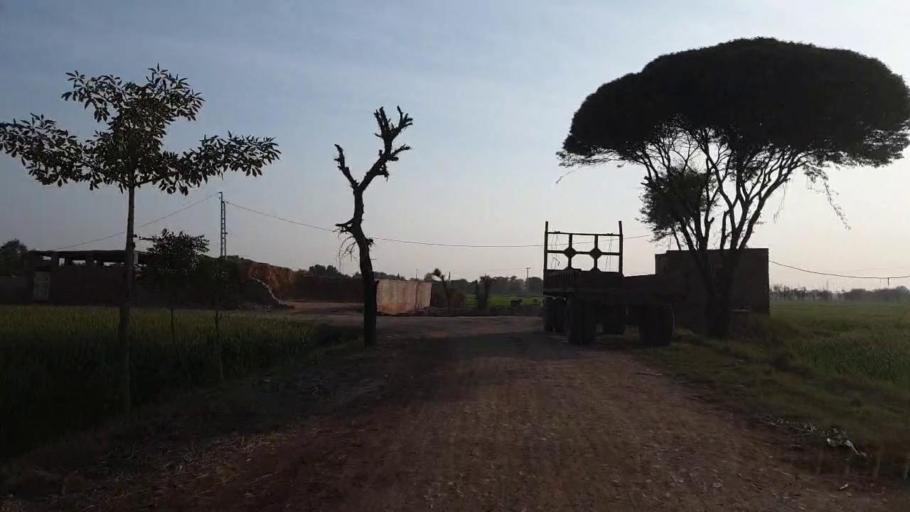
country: PK
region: Sindh
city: Matiari
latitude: 25.5886
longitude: 68.4696
